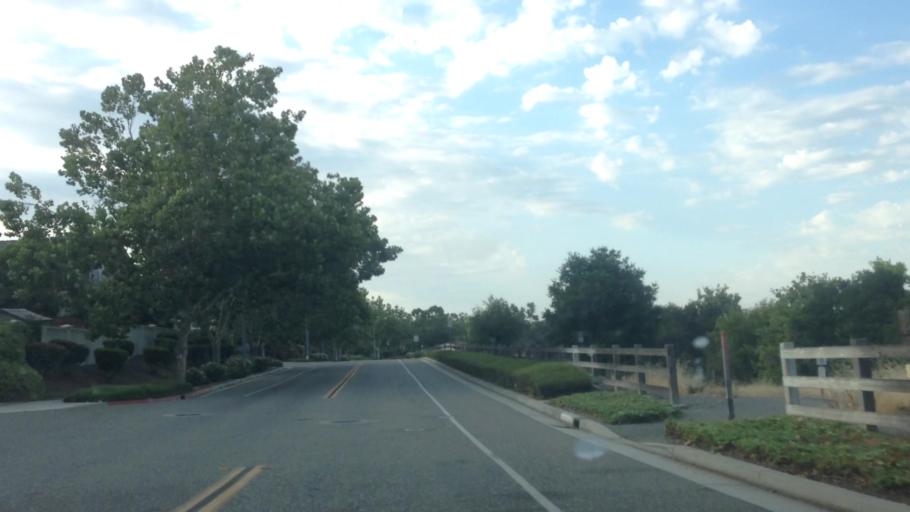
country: US
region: California
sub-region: Santa Clara County
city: Seven Trees
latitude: 37.2476
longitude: -121.7681
